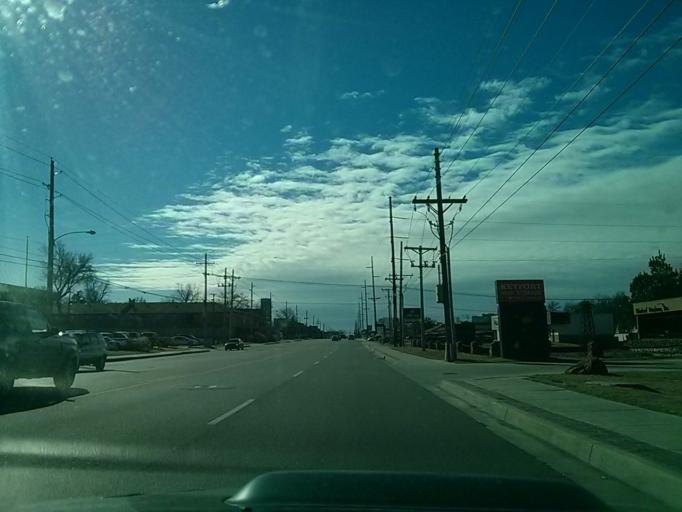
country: US
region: Oklahoma
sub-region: Tulsa County
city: Jenks
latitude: 36.0689
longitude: -95.9580
